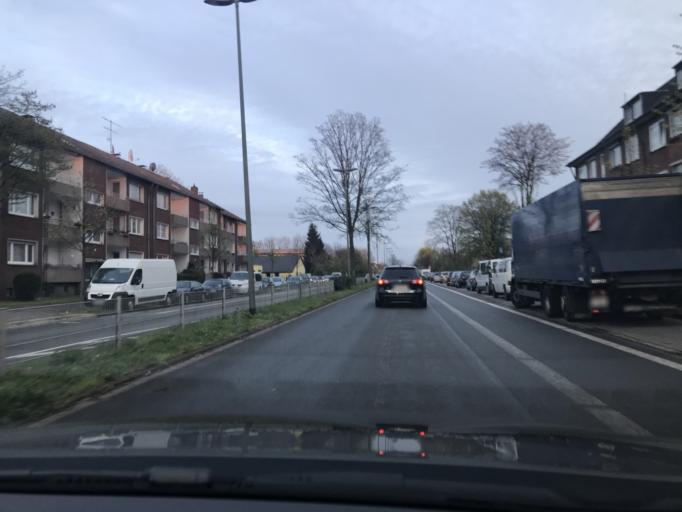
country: DE
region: North Rhine-Westphalia
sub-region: Regierungsbezirk Dusseldorf
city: Dinslaken
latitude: 51.5165
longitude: 6.7465
